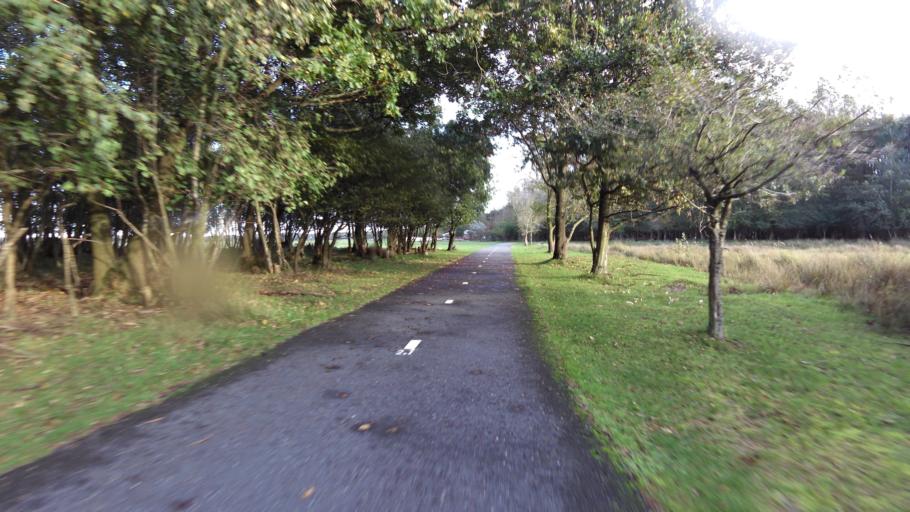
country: NL
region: South Holland
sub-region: Gemeente Noordwijkerhout
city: Noordwijkerhout
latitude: 52.2969
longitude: 4.5035
